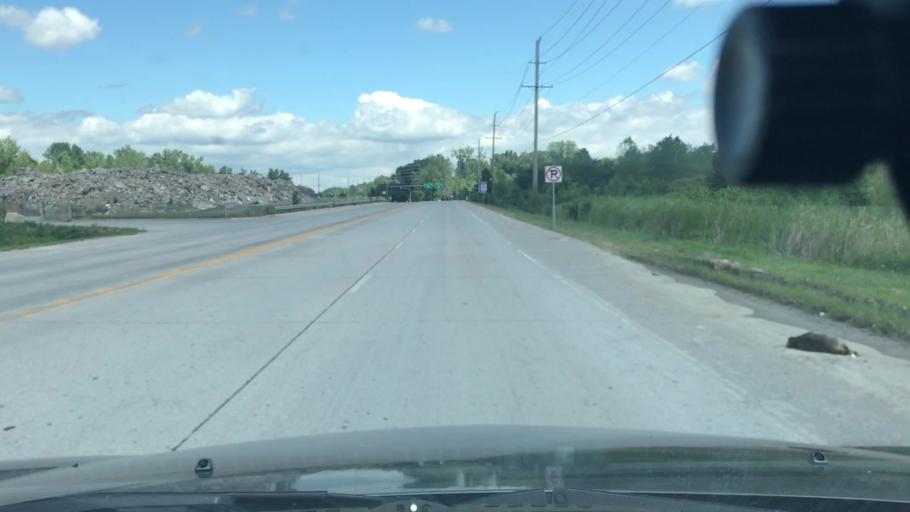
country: US
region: Missouri
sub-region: Saint Charles County
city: Saint Charles
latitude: 38.7518
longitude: -90.5055
